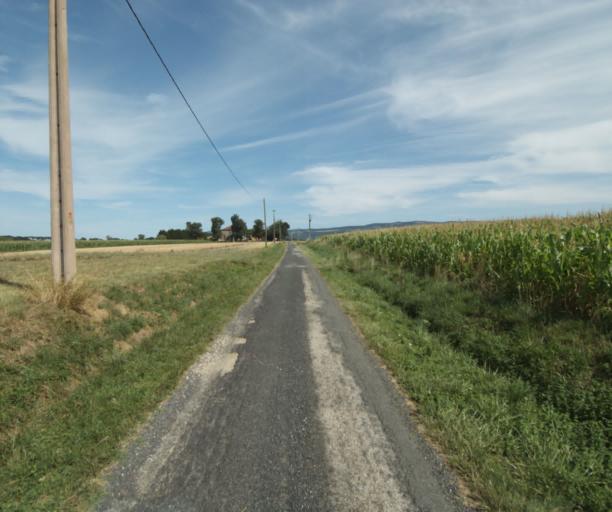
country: FR
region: Midi-Pyrenees
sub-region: Departement du Tarn
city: Soreze
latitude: 43.5114
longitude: 2.0728
